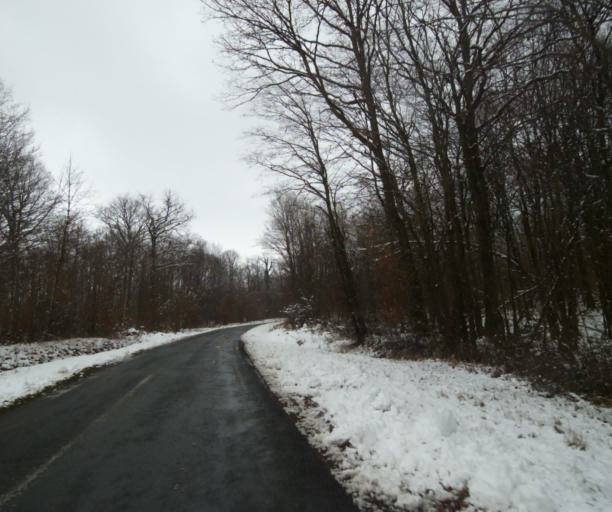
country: FR
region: Champagne-Ardenne
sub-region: Departement de la Haute-Marne
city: Laneuville-a-Remy
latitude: 48.4641
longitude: 4.8555
